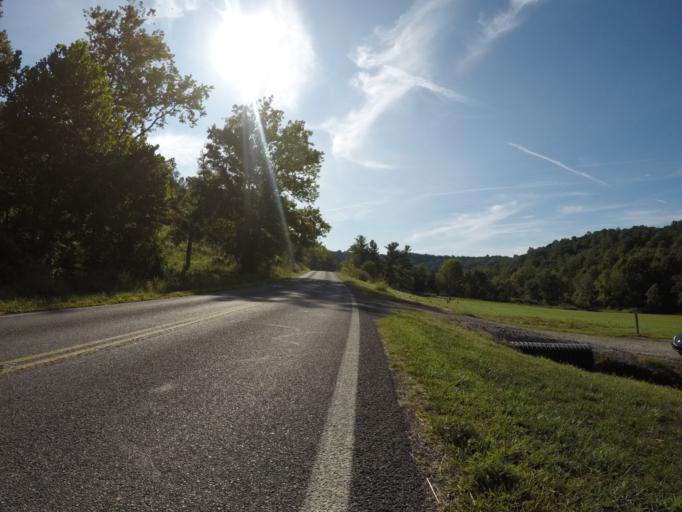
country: US
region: Ohio
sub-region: Lawrence County
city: Burlington
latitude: 38.4974
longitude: -82.5035
